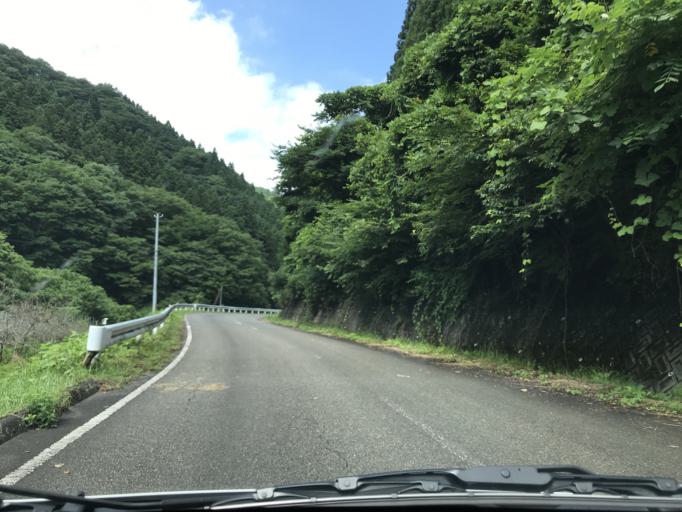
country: JP
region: Iwate
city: Tono
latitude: 39.0702
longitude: 141.4046
